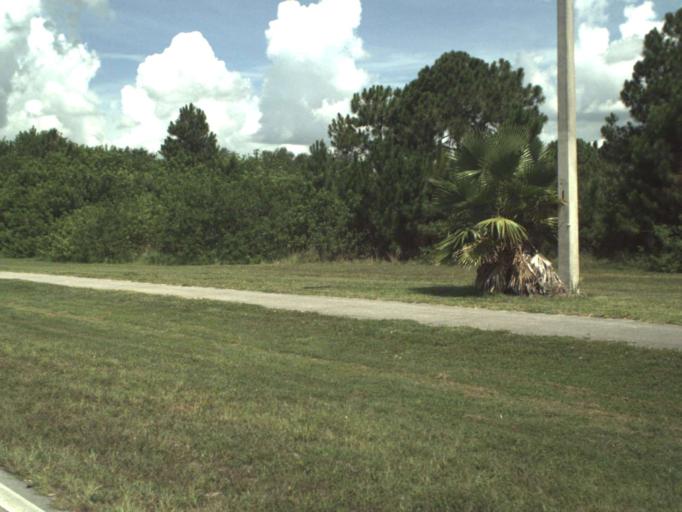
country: US
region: Florida
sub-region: Saint Lucie County
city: River Park
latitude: 27.3177
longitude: -80.3808
